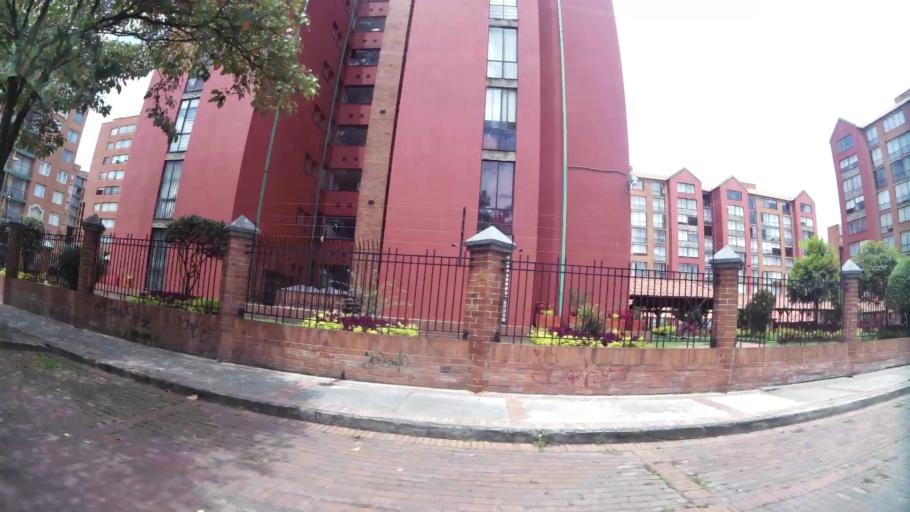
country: CO
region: Bogota D.C.
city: Bogota
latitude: 4.6404
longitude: -74.1025
